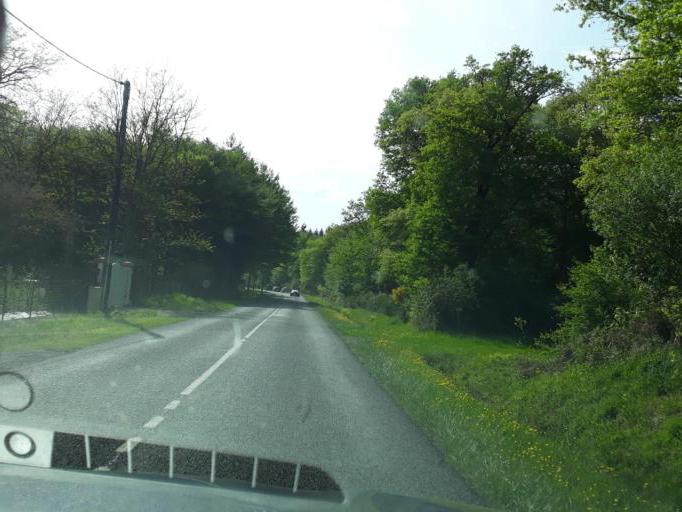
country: FR
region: Centre
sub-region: Departement du Loir-et-Cher
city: Dhuizon
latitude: 47.6596
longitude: 1.6640
